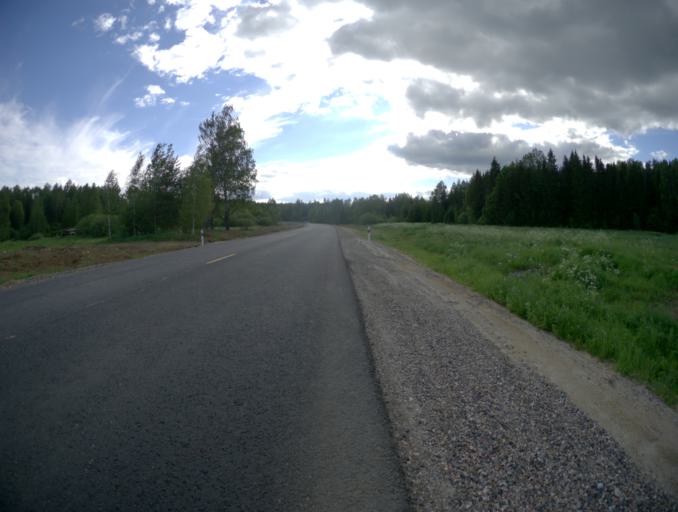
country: RU
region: Ivanovo
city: Kitovo
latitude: 56.8155
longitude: 41.2068
